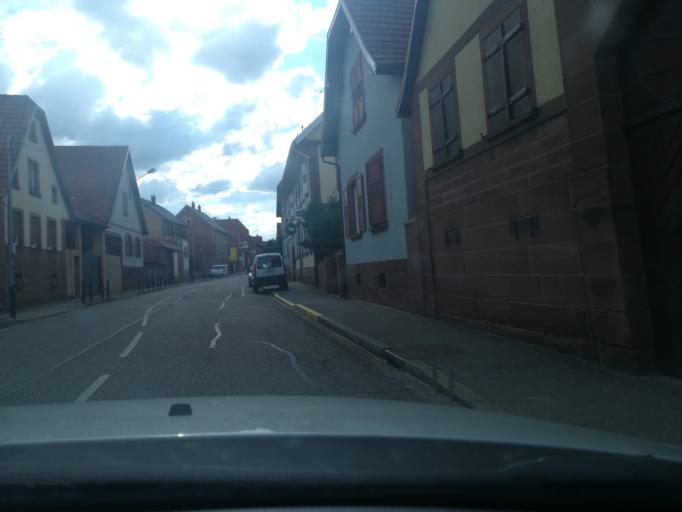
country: FR
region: Alsace
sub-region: Departement du Bas-Rhin
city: Obermodern-Zutzendorf
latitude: 48.8444
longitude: 7.5438
